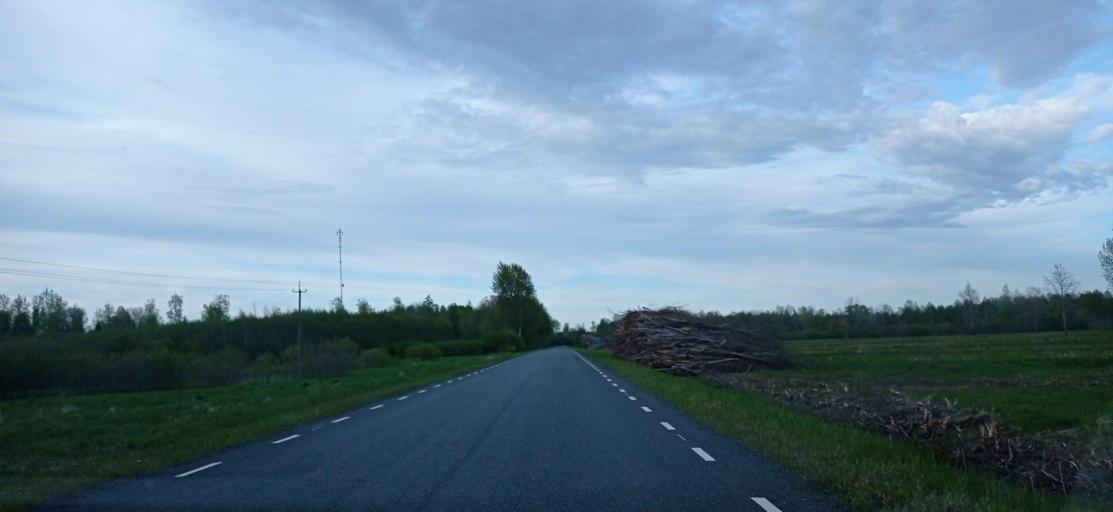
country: EE
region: Paernumaa
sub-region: Tootsi vald
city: Tootsi
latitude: 58.5626
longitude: 24.8007
